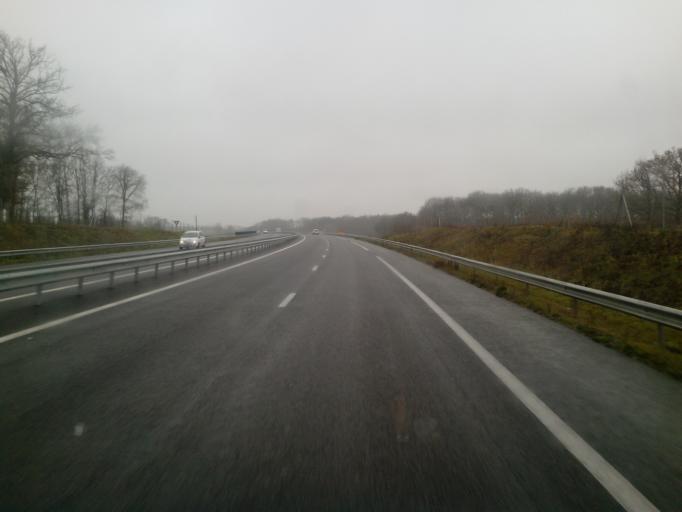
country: FR
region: Poitou-Charentes
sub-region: Departement de la Vienne
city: Terce
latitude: 46.4815
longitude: 0.5356
